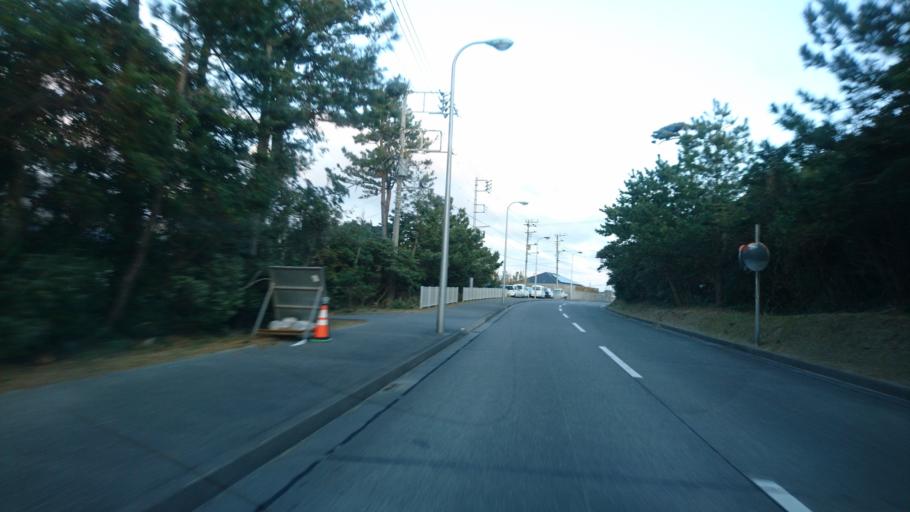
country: JP
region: Shizuoka
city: Shimoda
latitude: 34.3711
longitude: 139.2521
